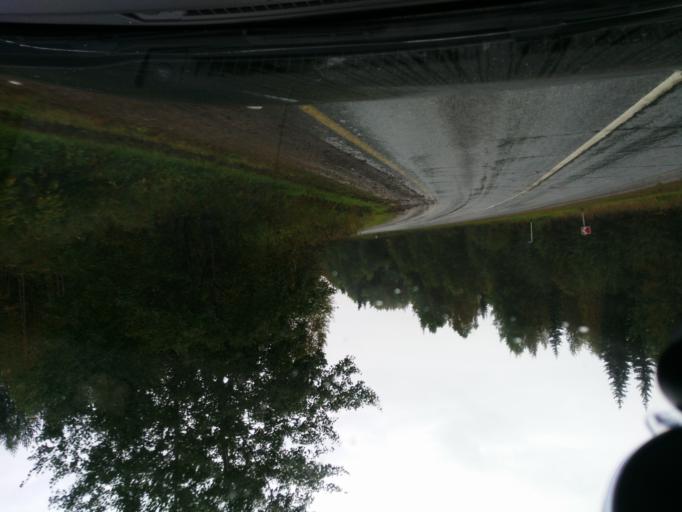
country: RU
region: Perm
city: Yugo-Kamskiy
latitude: 57.5277
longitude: 55.6842
